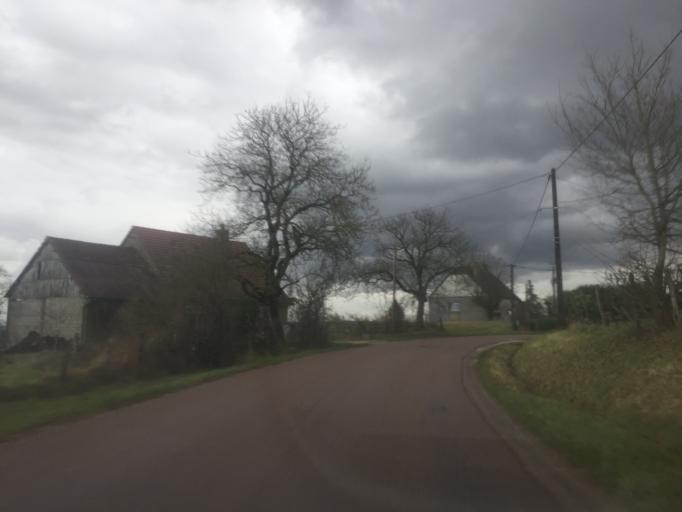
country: FR
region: Franche-Comte
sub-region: Departement de la Haute-Saone
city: Pesmes
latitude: 47.2240
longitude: 5.5406
